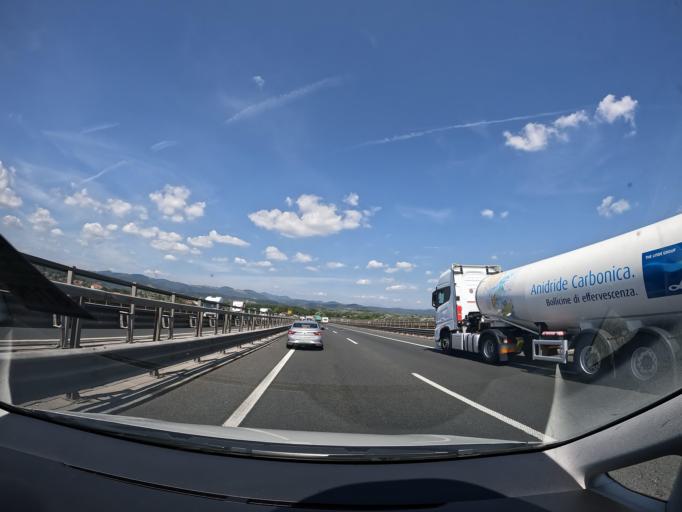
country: SI
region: Vrhnika
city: Verd
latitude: 45.9568
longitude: 14.3020
